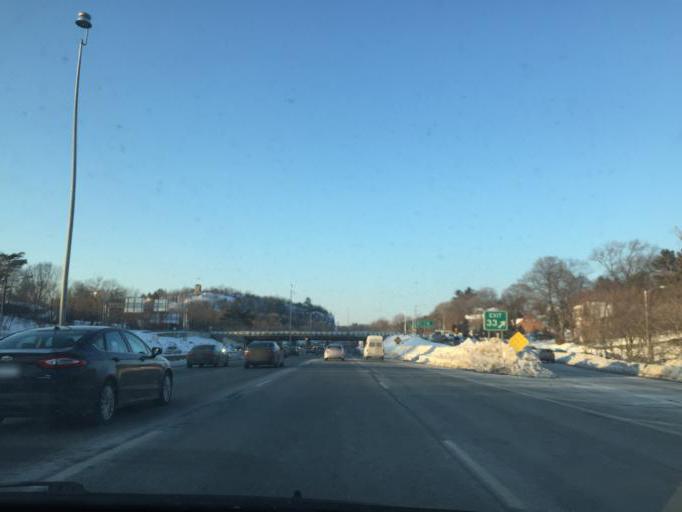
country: US
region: Massachusetts
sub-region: Middlesex County
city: Medford
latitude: 42.4265
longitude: -71.1031
